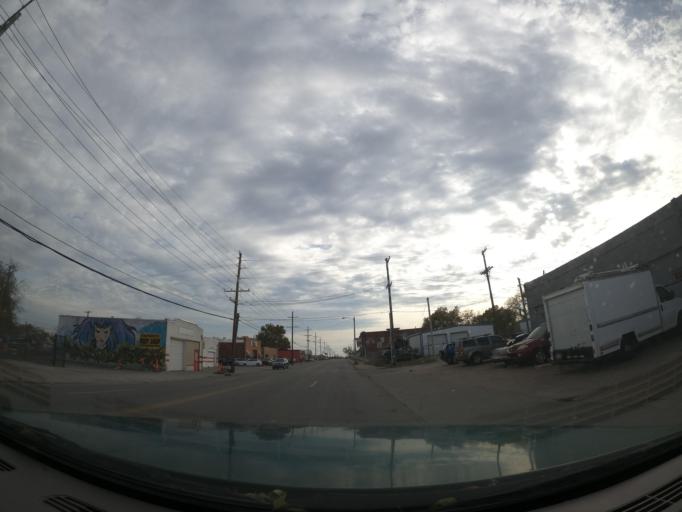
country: US
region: Oklahoma
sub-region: Tulsa County
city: Tulsa
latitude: 36.1655
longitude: -95.9582
